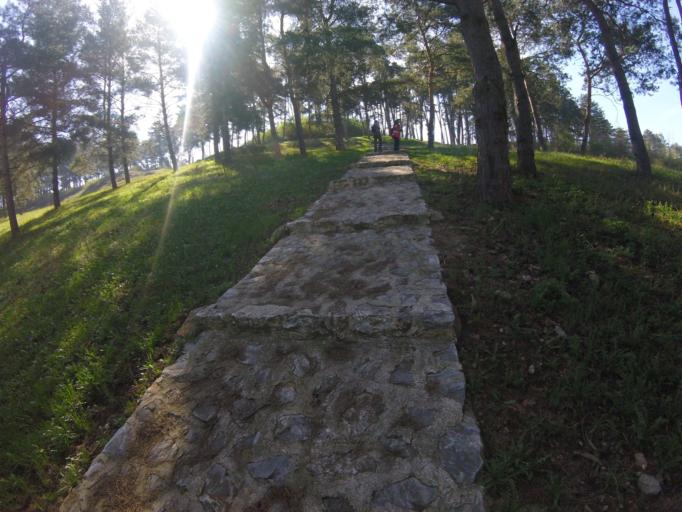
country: HU
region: Borsod-Abauj-Zemplen
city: Szendro
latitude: 48.4089
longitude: 20.7336
